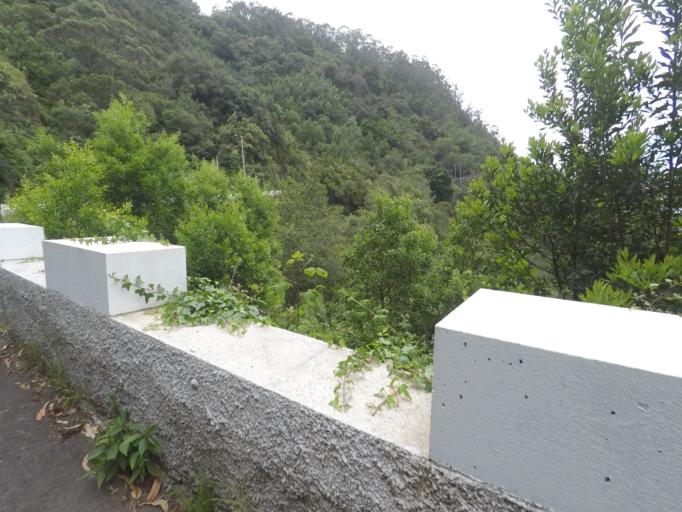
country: PT
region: Madeira
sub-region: Santana
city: Santana
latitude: 32.7913
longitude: -16.8627
